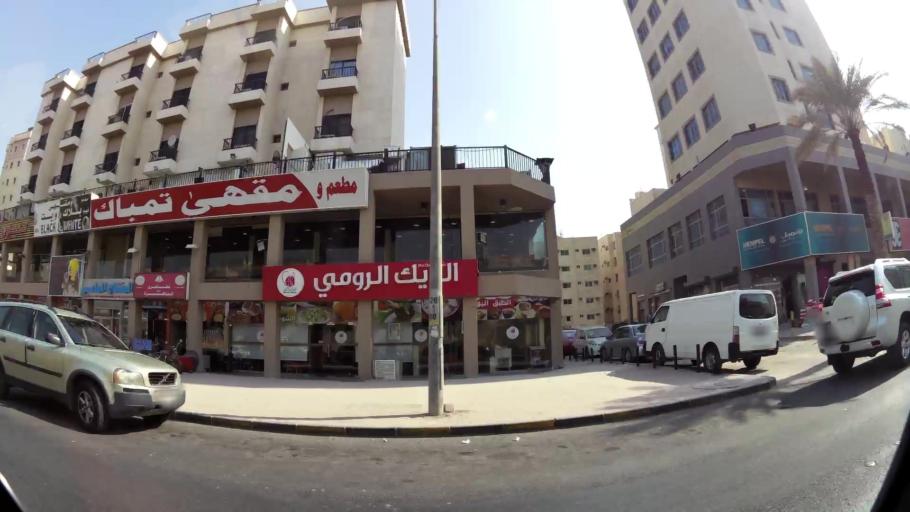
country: KW
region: Muhafazat Hawalli
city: Hawalli
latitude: 29.3410
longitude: 48.0141
